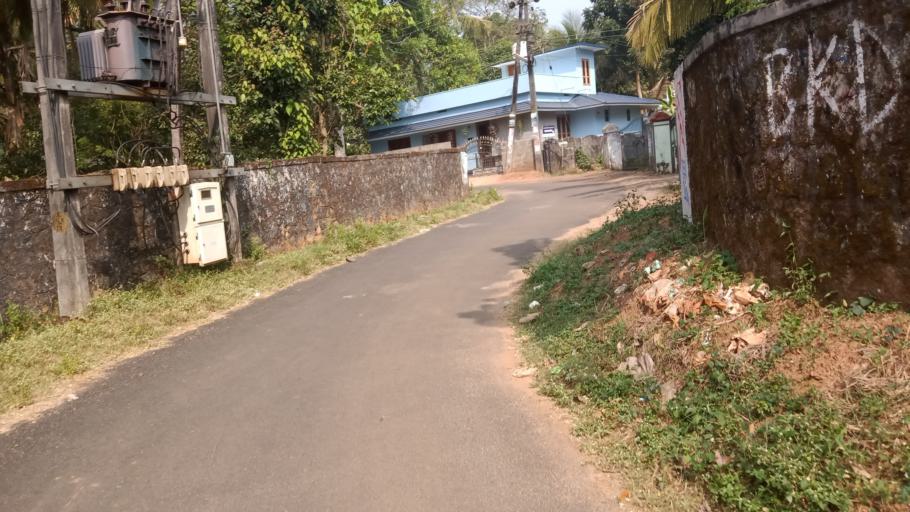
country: IN
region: Kerala
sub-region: Palakkad district
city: Cherpulassery
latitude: 10.8841
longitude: 76.3145
